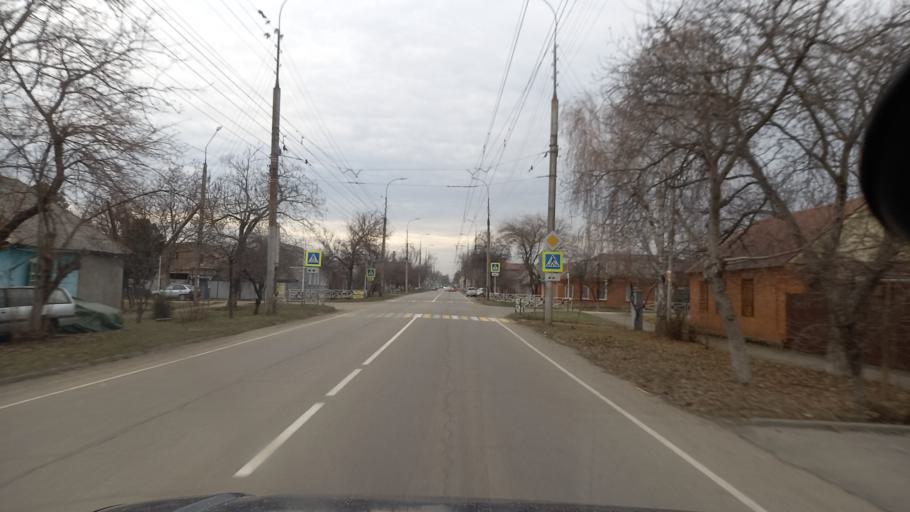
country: RU
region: Adygeya
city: Maykop
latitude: 44.6149
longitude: 40.1165
